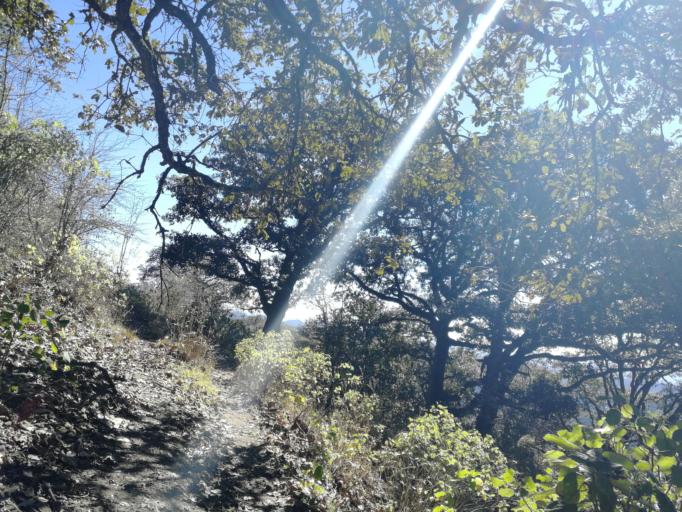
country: MX
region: San Luis Potosi
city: Zaragoza
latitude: 22.0081
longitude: -100.6160
